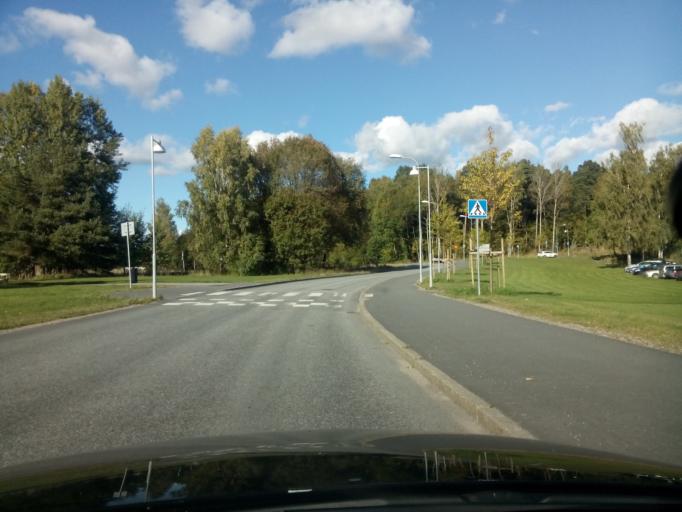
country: SE
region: Soedermanland
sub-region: Nykopings Kommun
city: Nykoping
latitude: 58.7674
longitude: 17.0084
